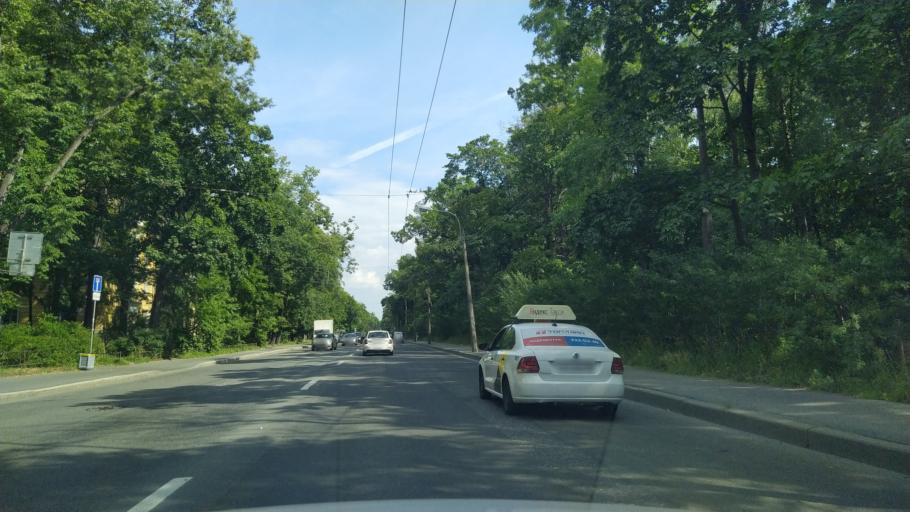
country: RU
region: Leningrad
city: Svetlanovskiy
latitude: 59.9968
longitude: 30.3391
